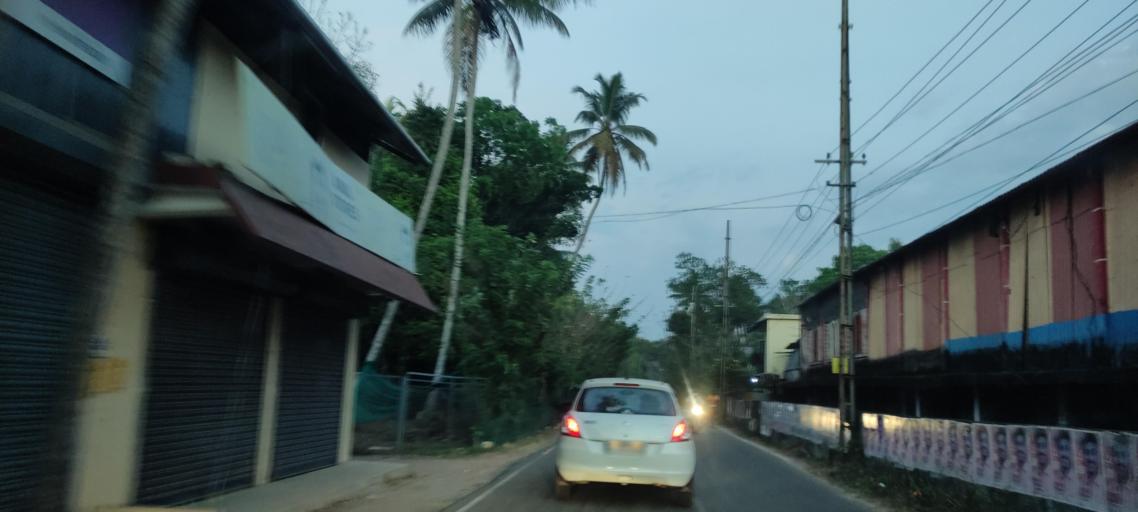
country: IN
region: Kerala
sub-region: Alappuzha
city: Kutiatodu
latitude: 9.7686
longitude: 76.3221
